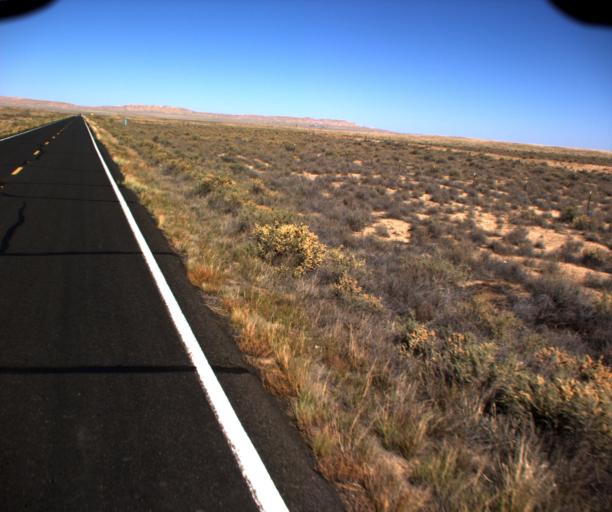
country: US
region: Arizona
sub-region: Navajo County
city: First Mesa
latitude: 35.6946
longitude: -110.5054
